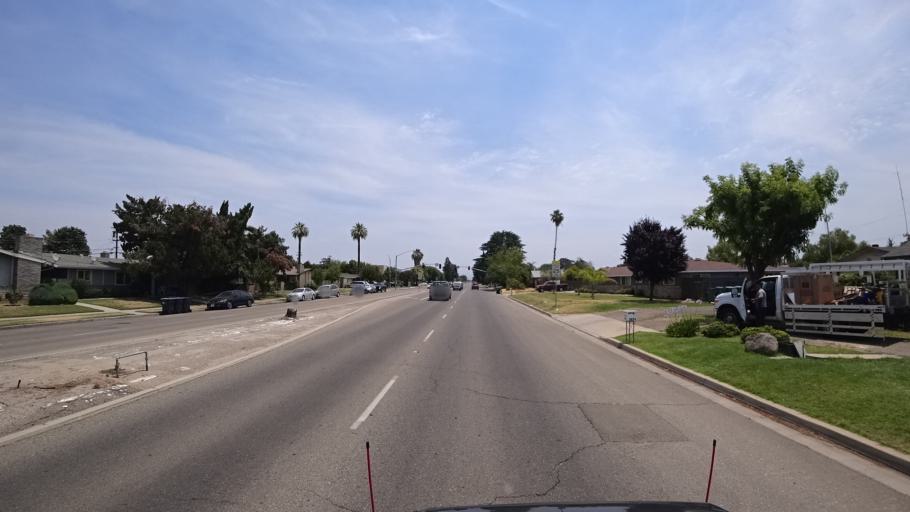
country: US
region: California
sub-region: Fresno County
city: Sunnyside
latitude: 36.7504
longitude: -119.7240
